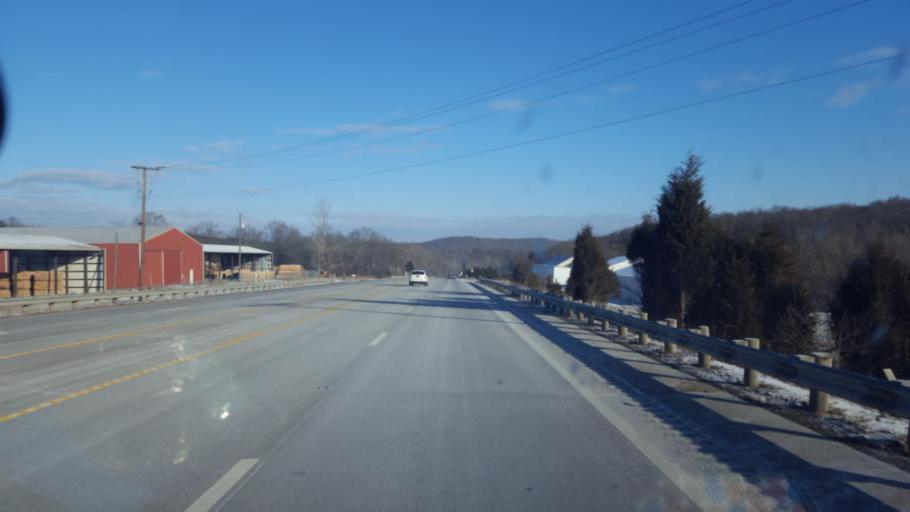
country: US
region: Ohio
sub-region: Pike County
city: Waverly
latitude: 39.1673
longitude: -82.9759
